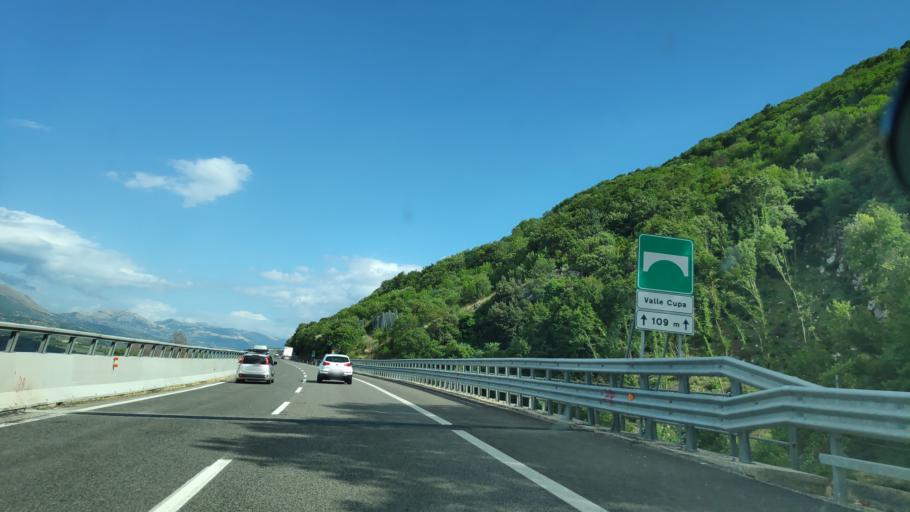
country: IT
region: Campania
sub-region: Provincia di Salerno
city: Sicignano degli Alburni
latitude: 40.5923
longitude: 15.3258
